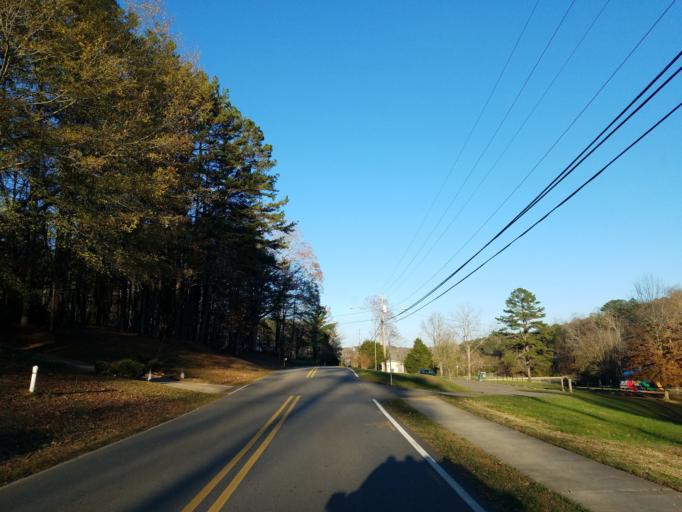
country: US
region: Georgia
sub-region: Cherokee County
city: Ball Ground
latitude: 34.3394
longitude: -84.3739
